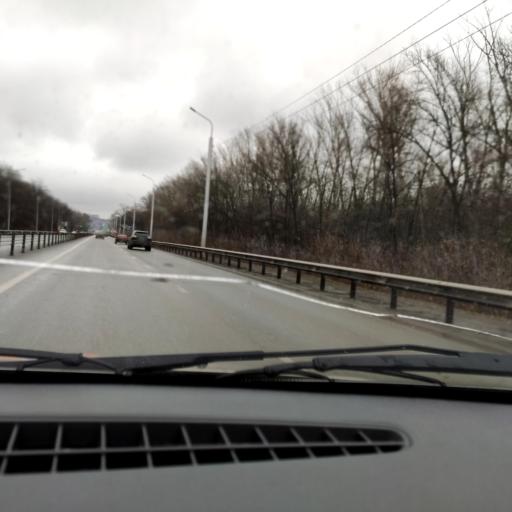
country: RU
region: Bashkortostan
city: Ufa
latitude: 54.7012
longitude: 55.9251
